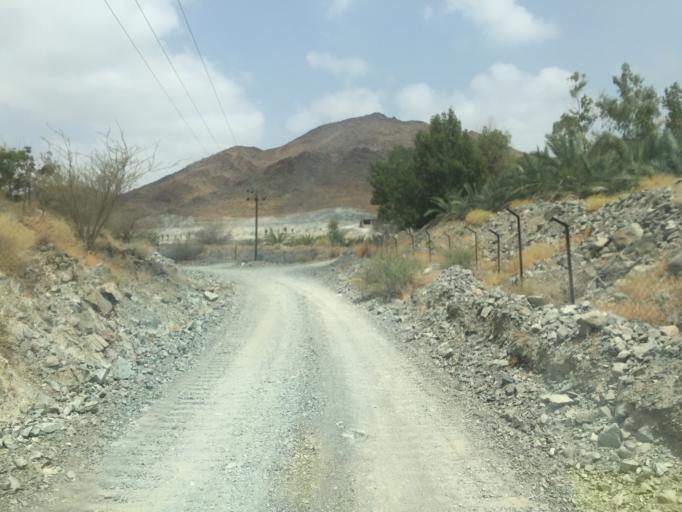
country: AE
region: Al Fujayrah
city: Al Fujayrah
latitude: 24.9324
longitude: 56.2174
